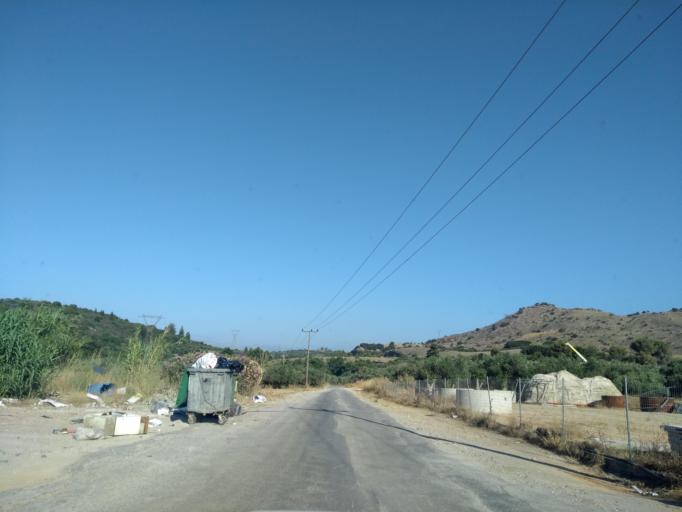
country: GR
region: Crete
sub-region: Nomos Chanias
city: Georgioupolis
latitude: 35.3670
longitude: 24.2334
